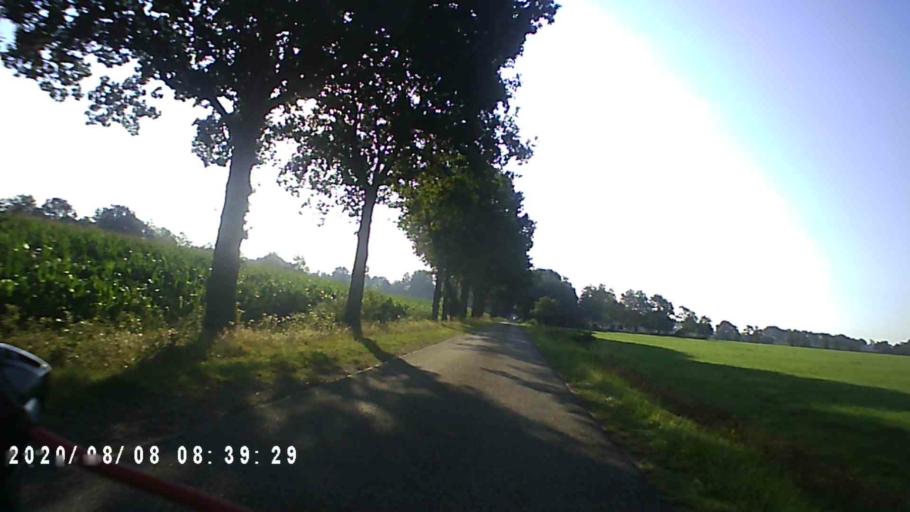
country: NL
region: Groningen
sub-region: Gemeente Leek
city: Leek
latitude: 53.0711
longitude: 6.3541
